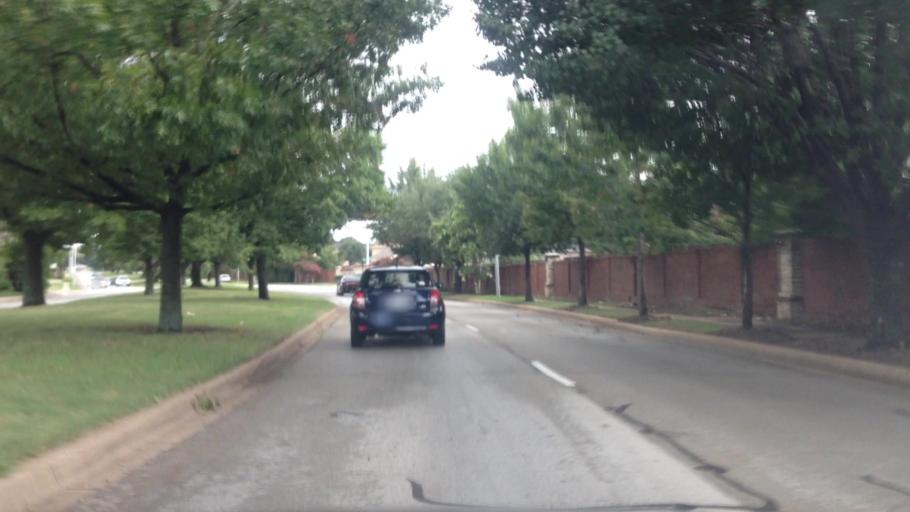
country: US
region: Texas
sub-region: Tarrant County
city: Edgecliff Village
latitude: 32.6386
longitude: -97.3956
